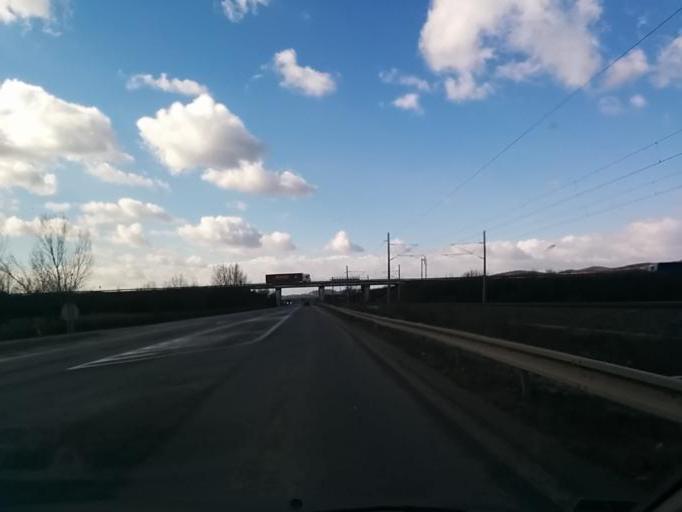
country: SK
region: Trenciansky
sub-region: Okres Trencin
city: Trencin
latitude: 48.8650
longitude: 17.9587
